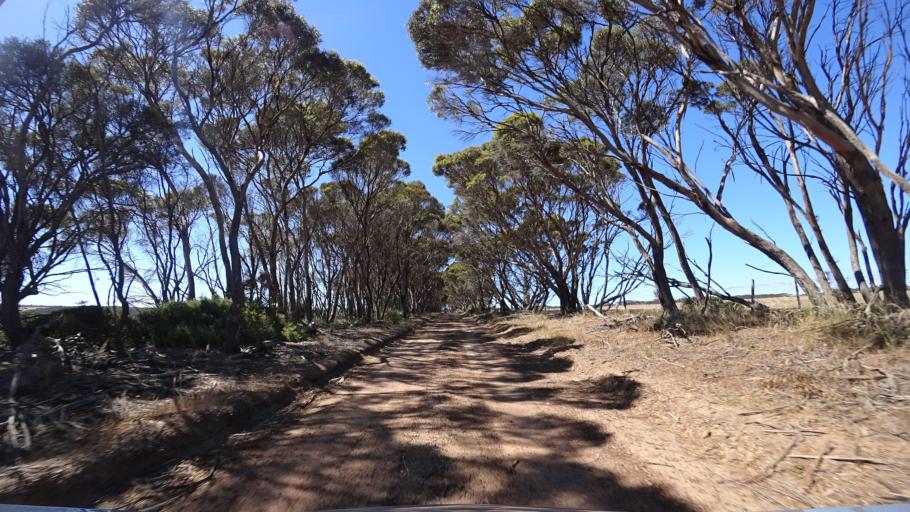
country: AU
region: South Australia
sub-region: Kangaroo Island
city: Kingscote
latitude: -35.7435
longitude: 137.7221
